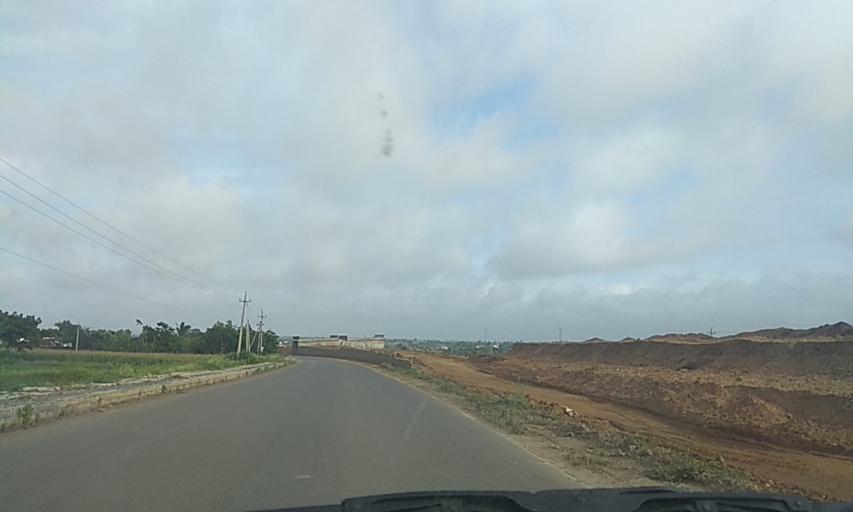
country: IN
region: Karnataka
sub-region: Haveri
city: Haveri
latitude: 14.8526
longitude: 75.3295
